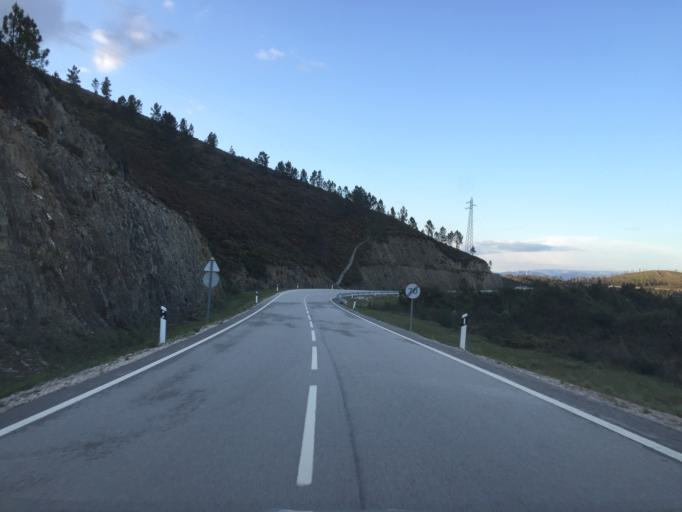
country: PT
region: Coimbra
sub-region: Gois
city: Gois
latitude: 40.1044
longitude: -8.0391
